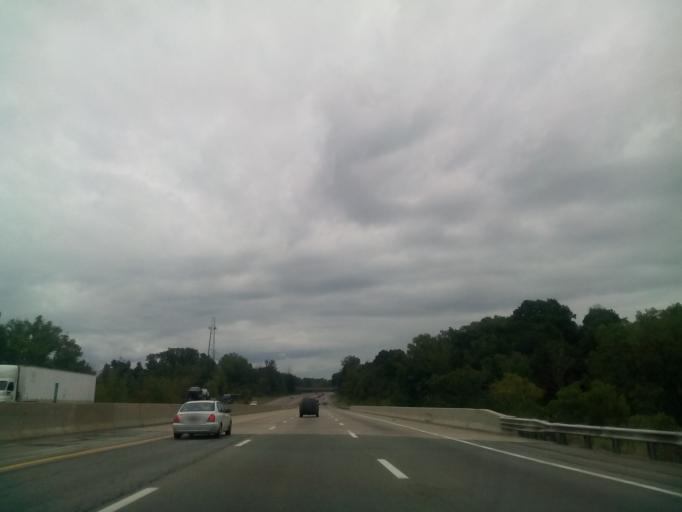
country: US
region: Ohio
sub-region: Lorain County
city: Vermilion
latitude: 41.3410
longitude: -82.3520
